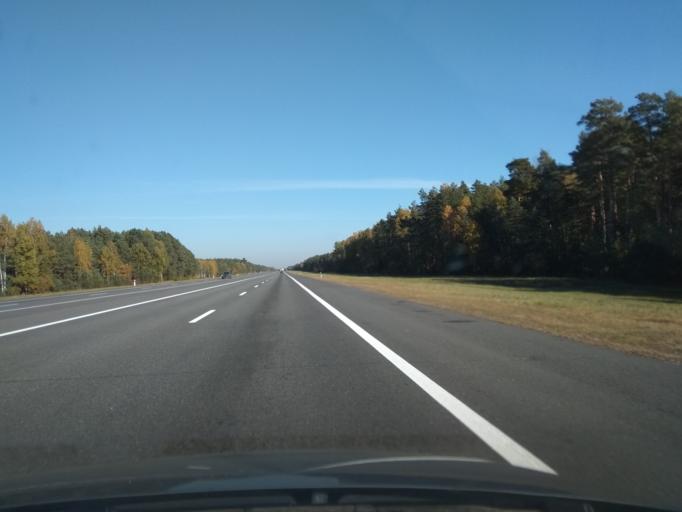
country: BY
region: Brest
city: Ivatsevichy
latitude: 52.7506
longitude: 25.5005
